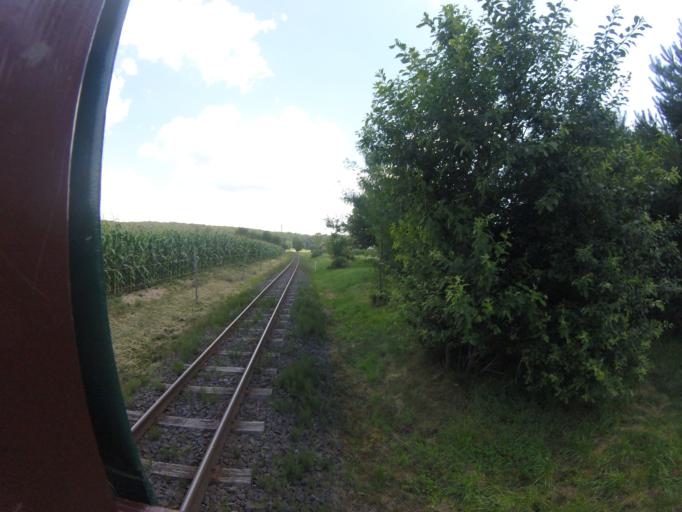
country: HU
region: Zala
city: Letenye
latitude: 46.5684
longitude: 16.6851
